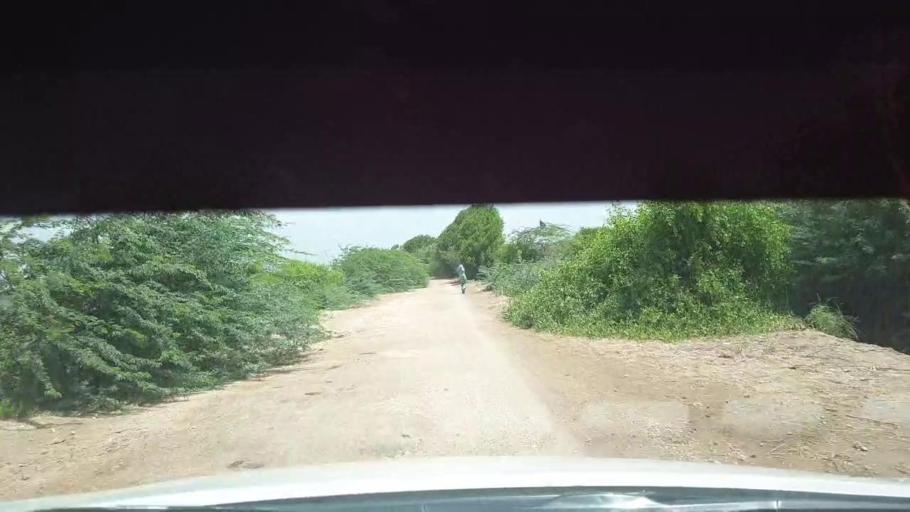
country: PK
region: Sindh
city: Kadhan
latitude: 24.5116
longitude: 68.9757
